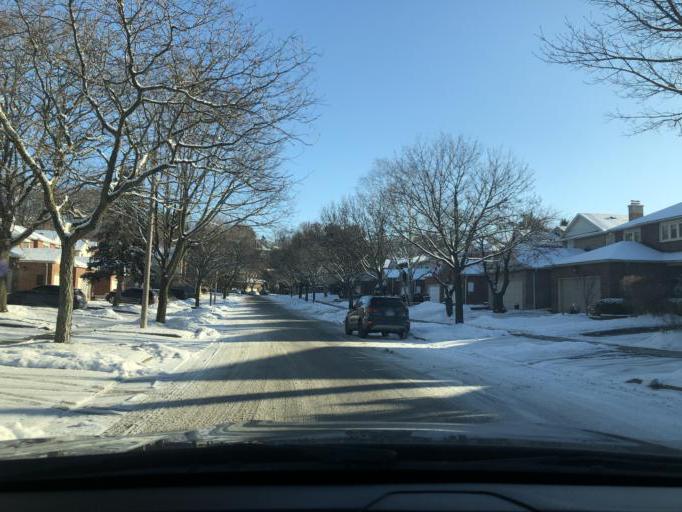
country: CA
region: Ontario
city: Pickering
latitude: 43.7863
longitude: -79.1323
